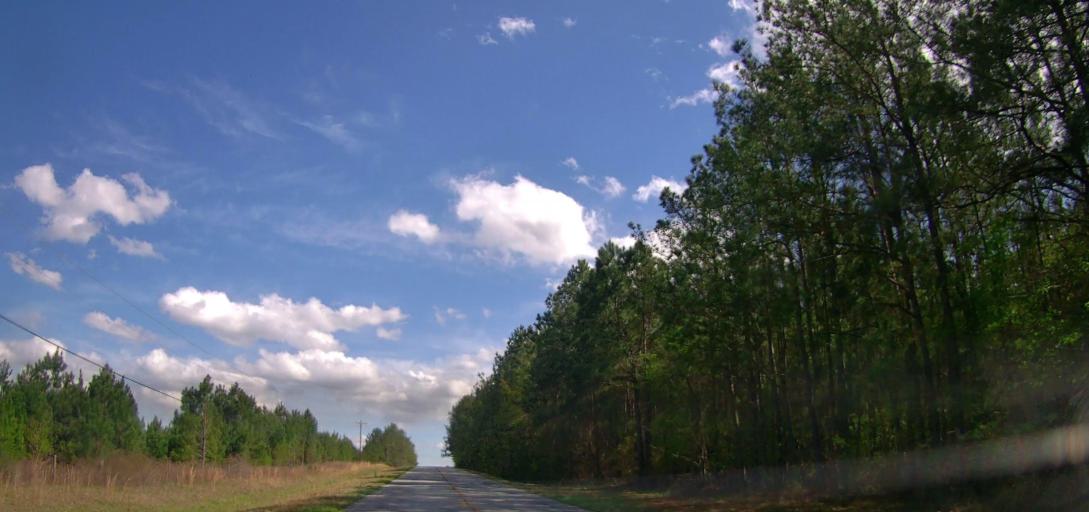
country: US
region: Georgia
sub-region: Wilkinson County
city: Gordon
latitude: 32.8381
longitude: -83.4376
